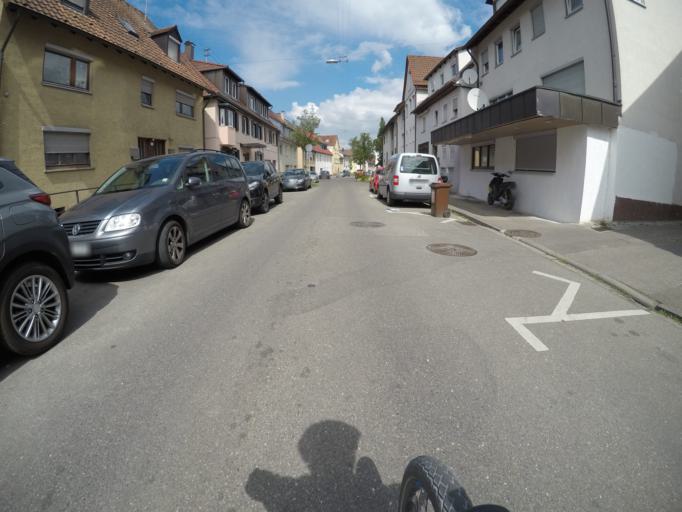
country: DE
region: Baden-Wuerttemberg
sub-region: Regierungsbezirk Stuttgart
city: Wendlingen am Neckar
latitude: 48.6757
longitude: 9.3846
